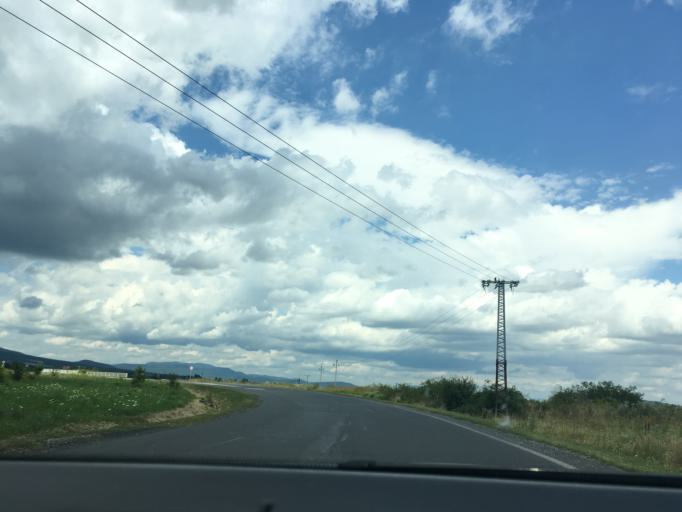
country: HU
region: Borsod-Abauj-Zemplen
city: Satoraljaujhely
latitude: 48.4060
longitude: 21.6622
